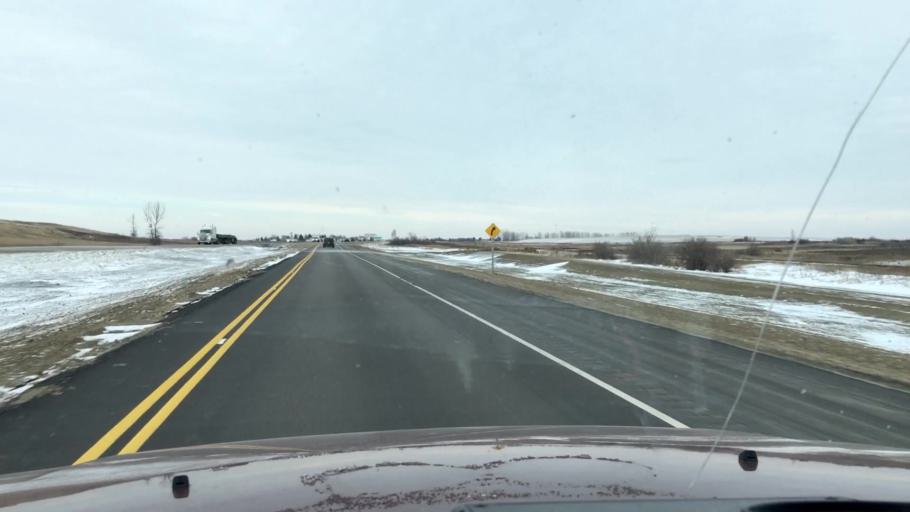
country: CA
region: Saskatchewan
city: Moose Jaw
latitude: 50.8622
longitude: -105.5906
